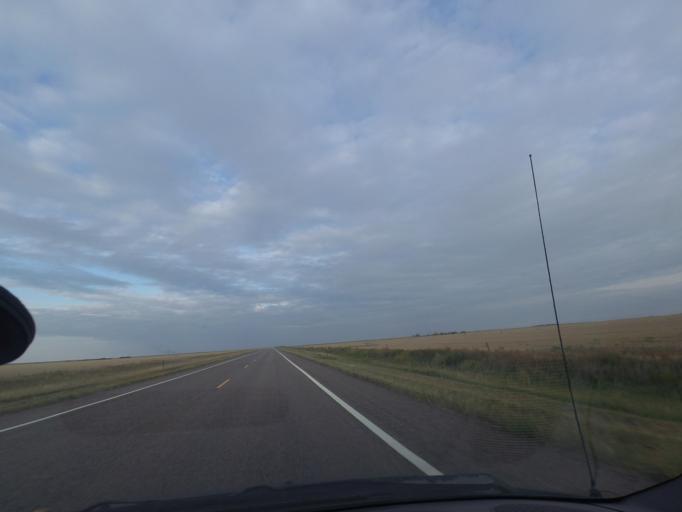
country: US
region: Colorado
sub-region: Yuma County
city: Wray
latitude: 39.7462
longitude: -102.2290
